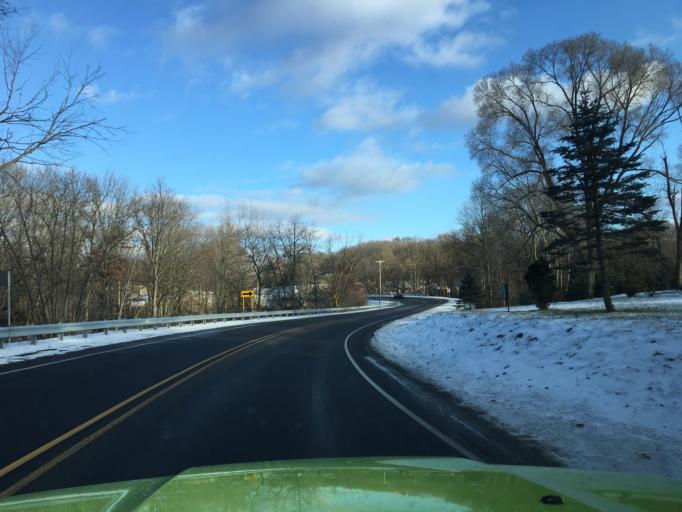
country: US
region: Michigan
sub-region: Montcalm County
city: Greenville
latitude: 43.2062
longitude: -85.2722
